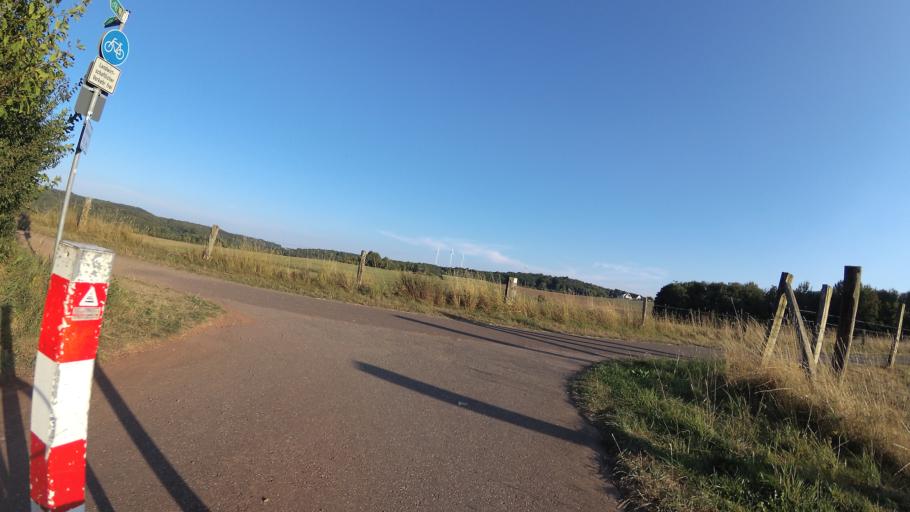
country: DE
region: Saarland
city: Oberthal
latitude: 49.5543
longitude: 7.0656
